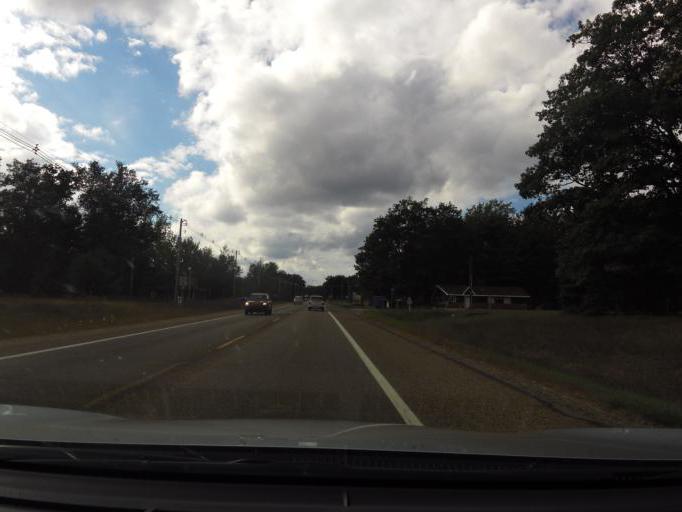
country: US
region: Michigan
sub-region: Roscommon County
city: Prudenville
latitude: 44.3056
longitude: -84.6323
